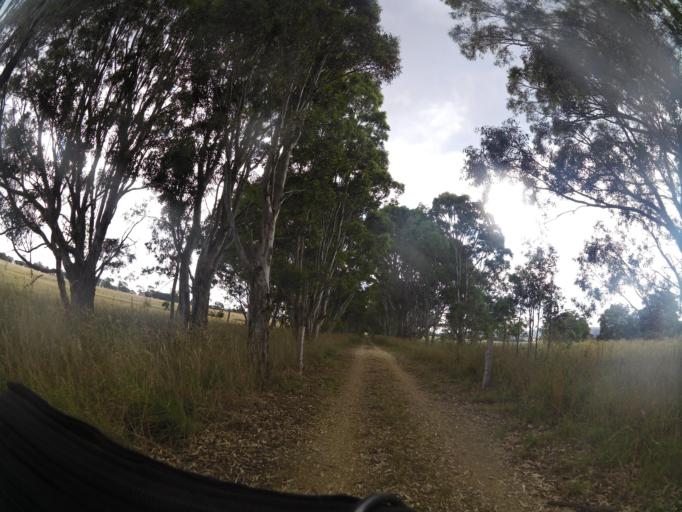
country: AU
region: Victoria
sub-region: Wellington
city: Heyfield
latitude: -38.0207
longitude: 146.6800
